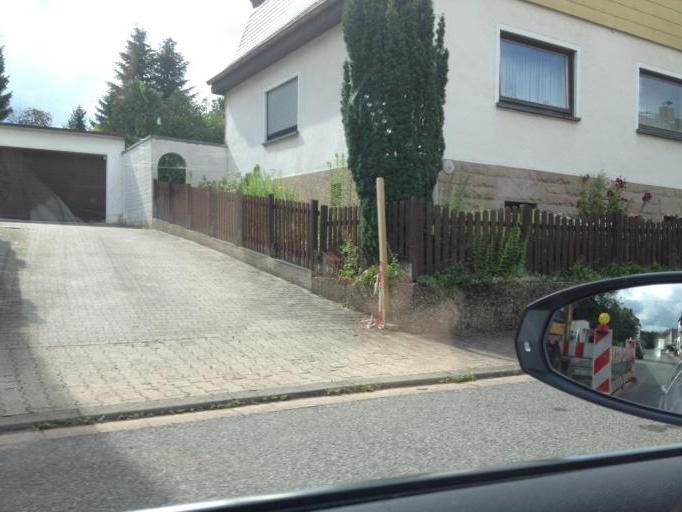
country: DE
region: Saarland
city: Schiffweiler
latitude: 49.3651
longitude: 7.1333
